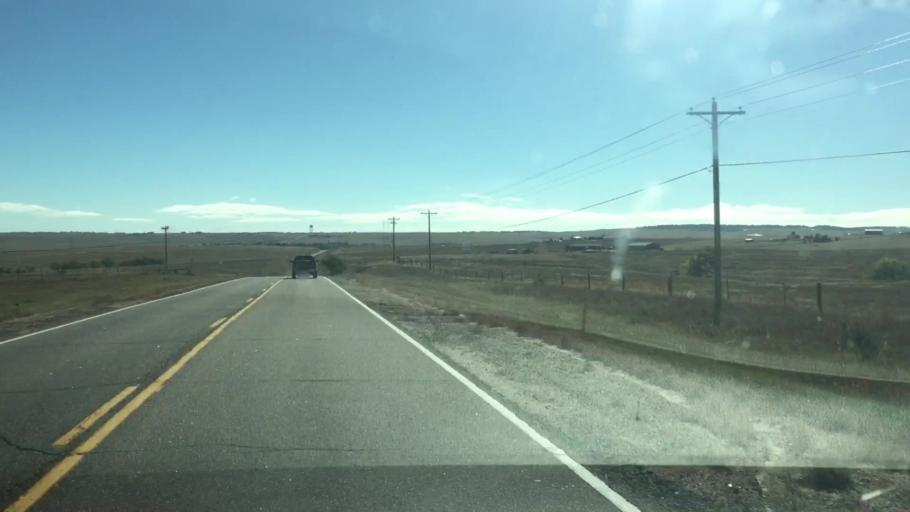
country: US
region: Colorado
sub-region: Elbert County
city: Kiowa
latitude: 39.3525
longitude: -104.4979
